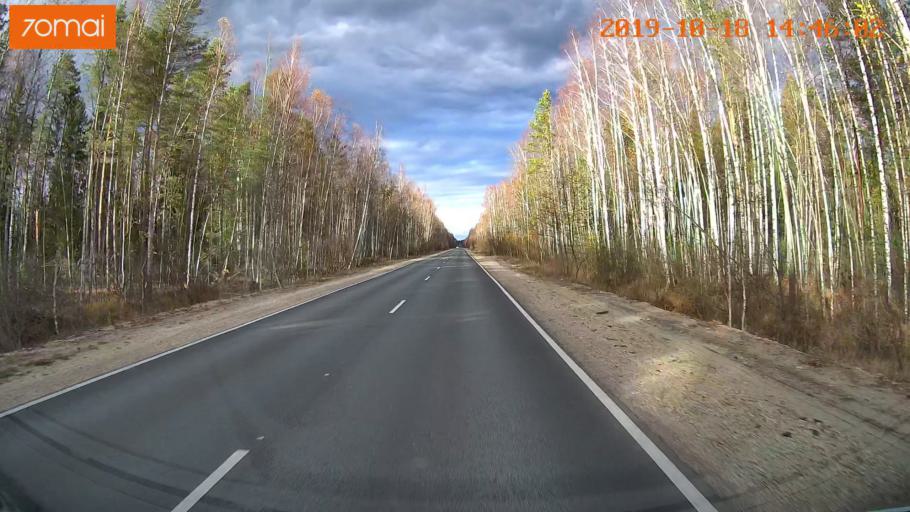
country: RU
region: Vladimir
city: Velikodvorskiy
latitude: 55.3646
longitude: 40.6801
